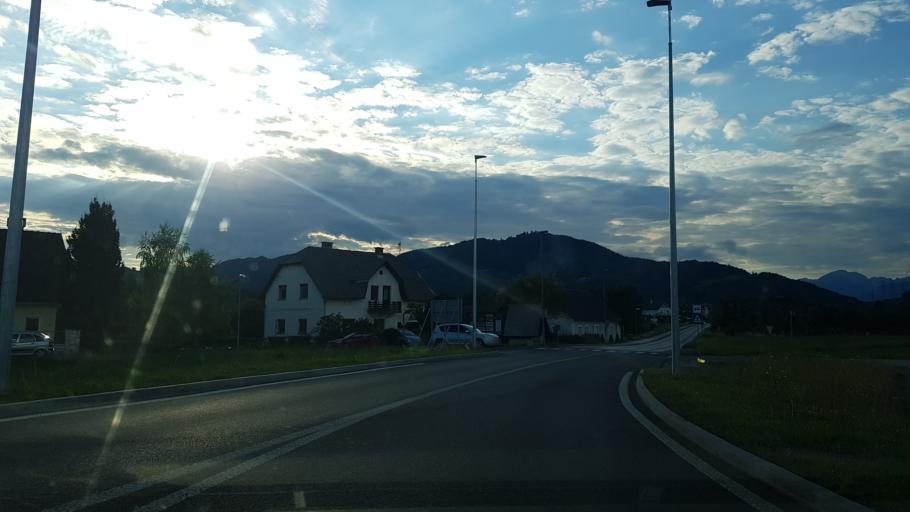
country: SI
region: Kranj
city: Zgornje Bitnje
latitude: 46.2217
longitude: 14.3404
